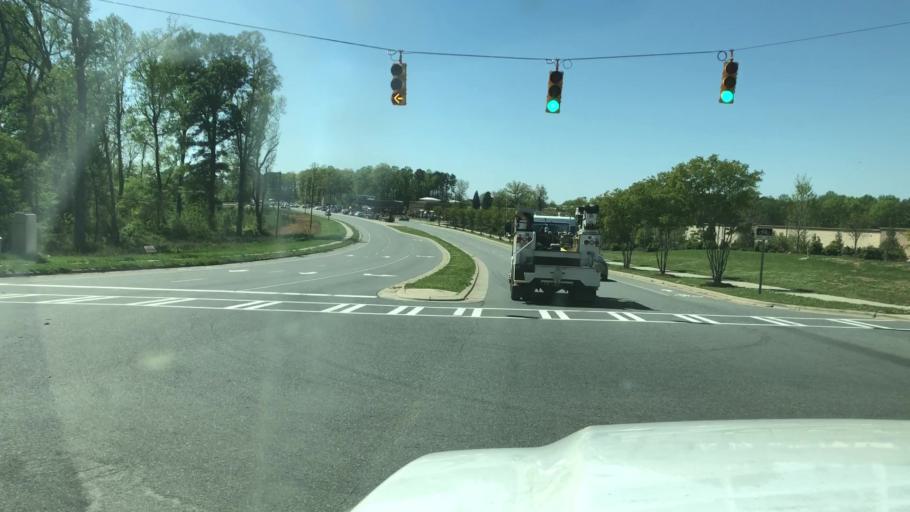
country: US
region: North Carolina
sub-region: Mecklenburg County
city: Huntersville
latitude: 35.3693
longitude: -80.8268
